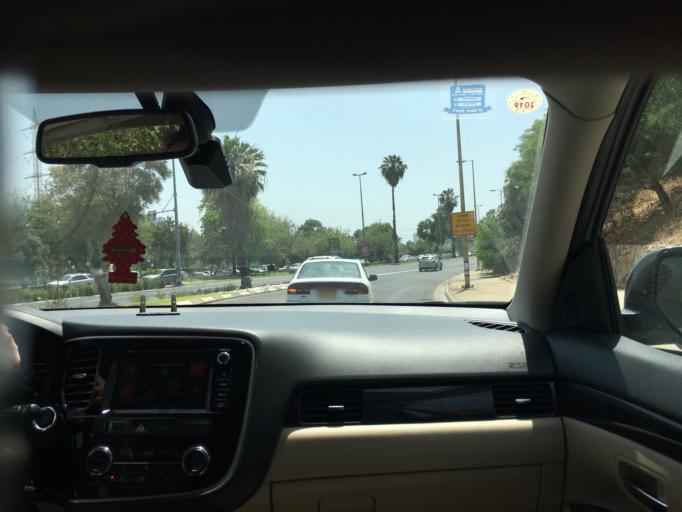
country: IL
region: Tel Aviv
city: Ramat Gan
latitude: 32.1019
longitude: 34.8013
